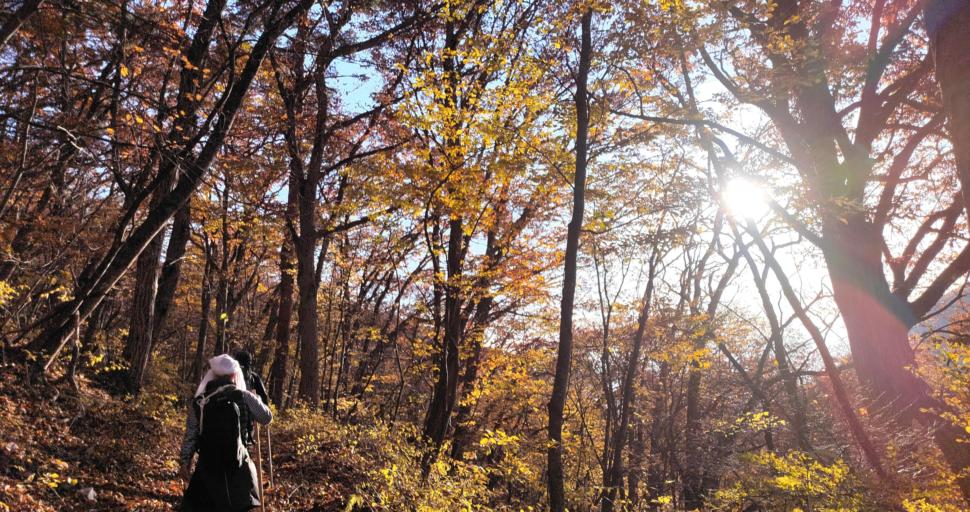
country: JP
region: Nagano
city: Komoro
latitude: 36.3830
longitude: 138.4382
